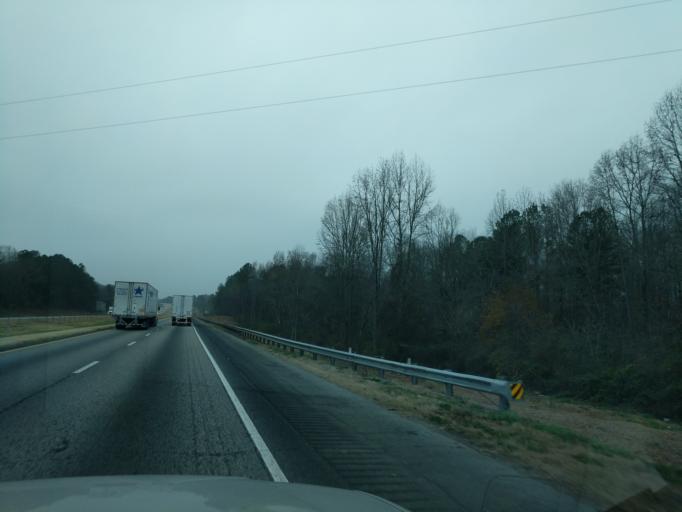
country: US
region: Georgia
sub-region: Banks County
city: Maysville
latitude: 34.2239
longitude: -83.5128
